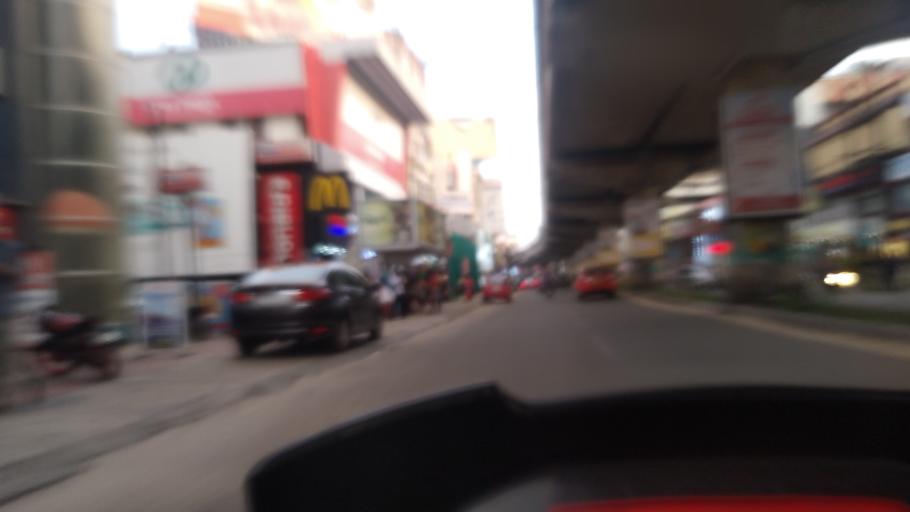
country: IN
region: Kerala
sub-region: Ernakulam
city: Cochin
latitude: 9.9809
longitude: 76.2831
